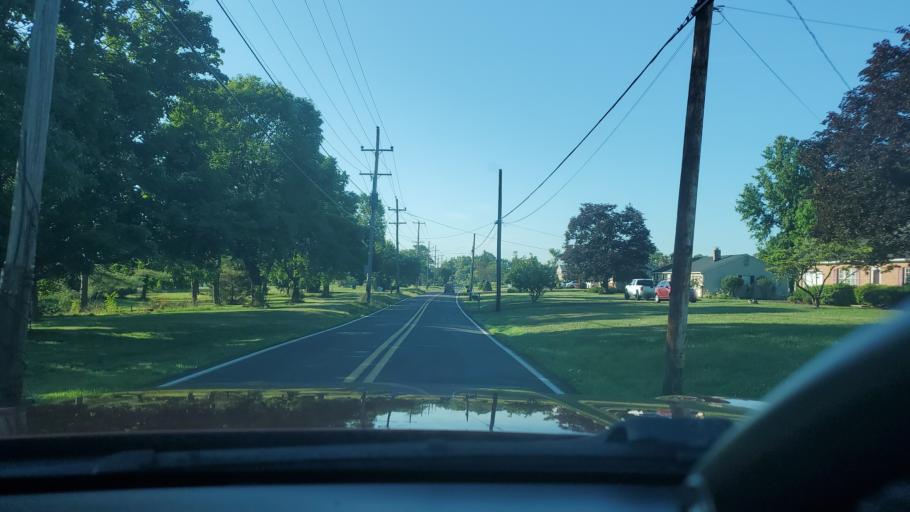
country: US
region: Pennsylvania
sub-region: Montgomery County
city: Woxall
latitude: 40.3025
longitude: -75.4433
